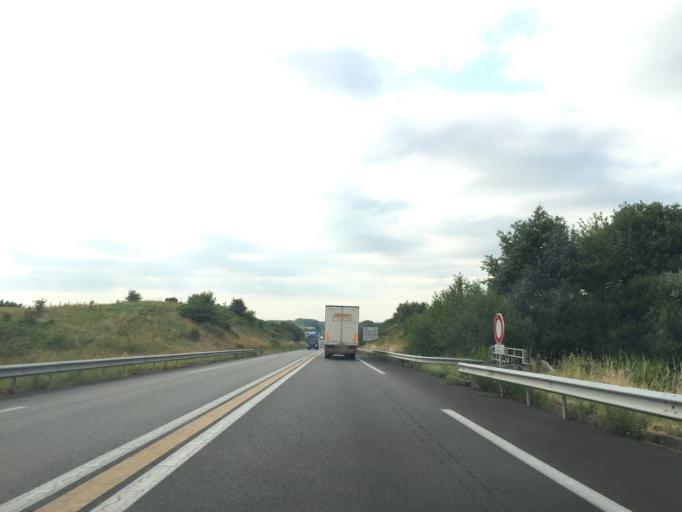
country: FR
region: Auvergne
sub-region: Departement de l'Allier
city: Diou
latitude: 46.5210
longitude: 3.7348
